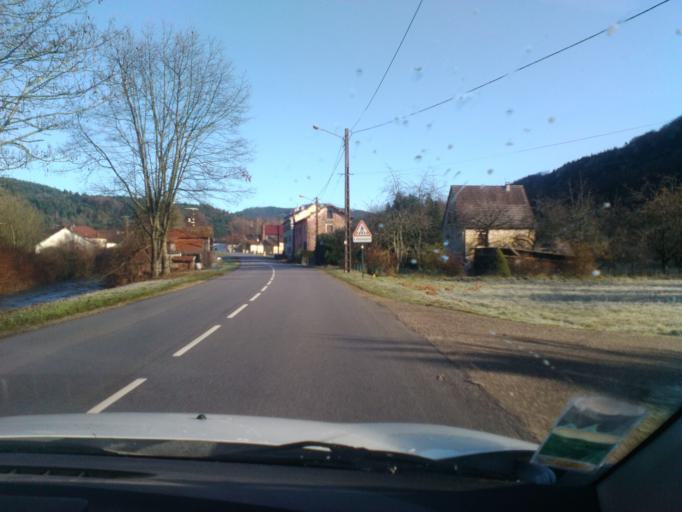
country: FR
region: Lorraine
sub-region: Departement des Vosges
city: Plombieres-les-Bains
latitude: 47.9360
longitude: 6.5040
